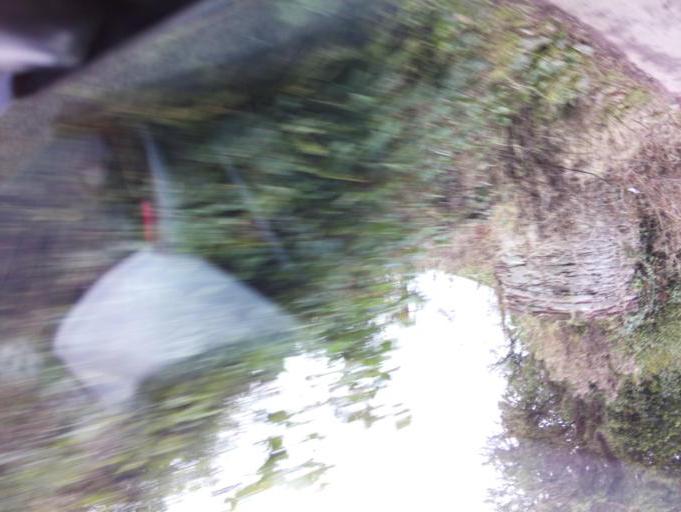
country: GB
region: England
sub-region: Devon
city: Kingsbridge
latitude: 50.2817
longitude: -3.7180
